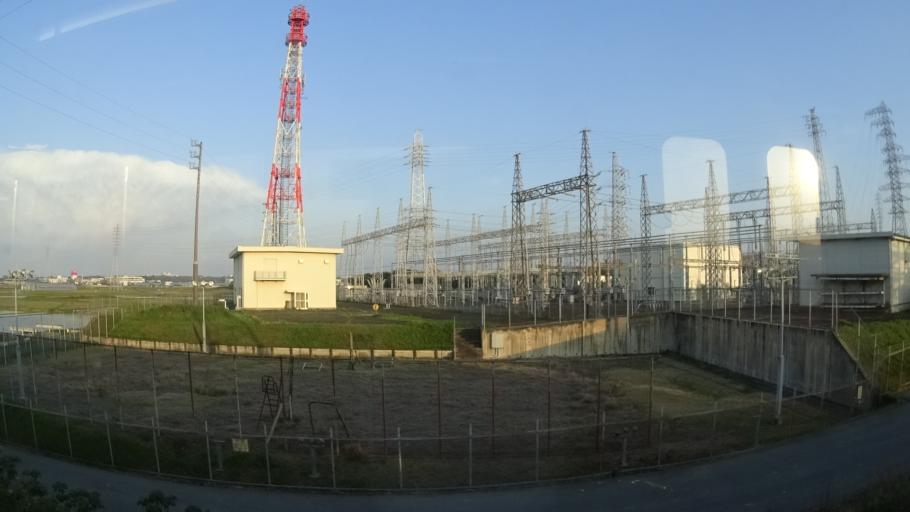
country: JP
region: Aichi
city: Toyohashi
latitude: 34.7121
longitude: 137.3750
